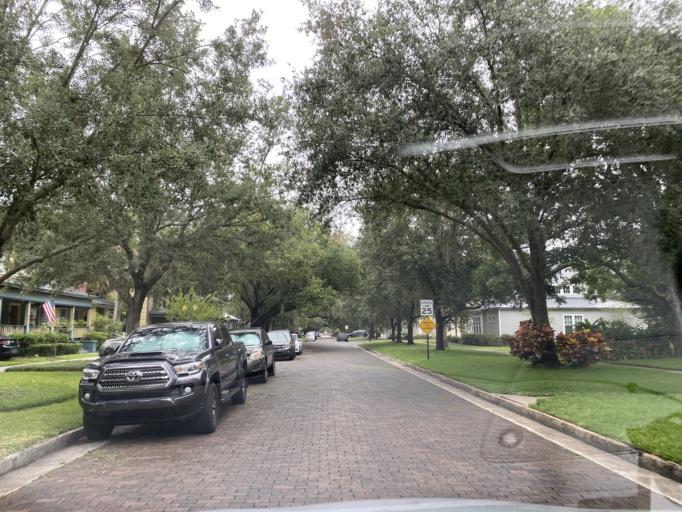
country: US
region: Florida
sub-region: Seminole County
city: Sanford
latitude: 28.8047
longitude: -81.2670
